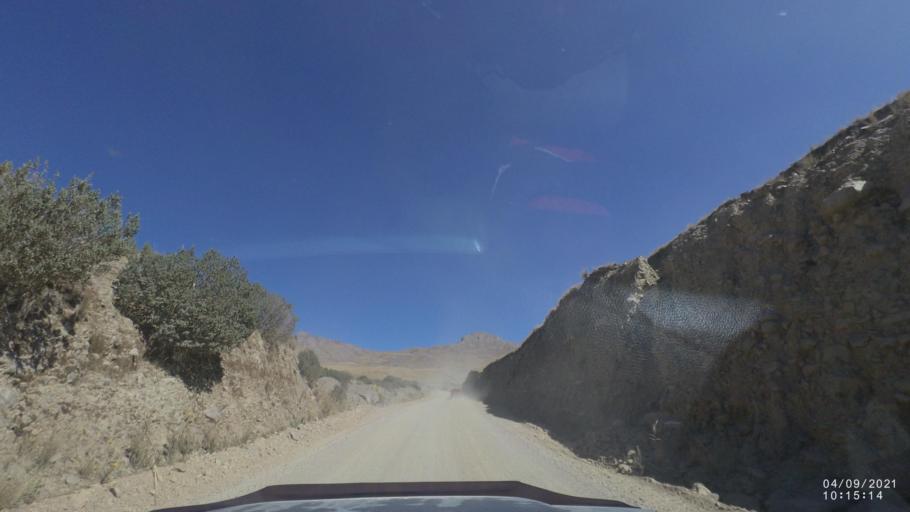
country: BO
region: Cochabamba
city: Sipe Sipe
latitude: -17.3268
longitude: -66.4137
